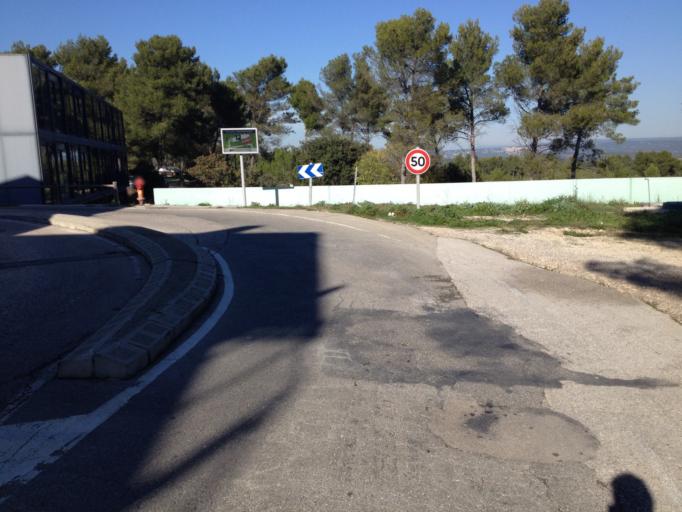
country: FR
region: Provence-Alpes-Cote d'Azur
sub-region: Departement des Bouches-du-Rhone
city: Ventabren
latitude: 43.4918
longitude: 5.3356
